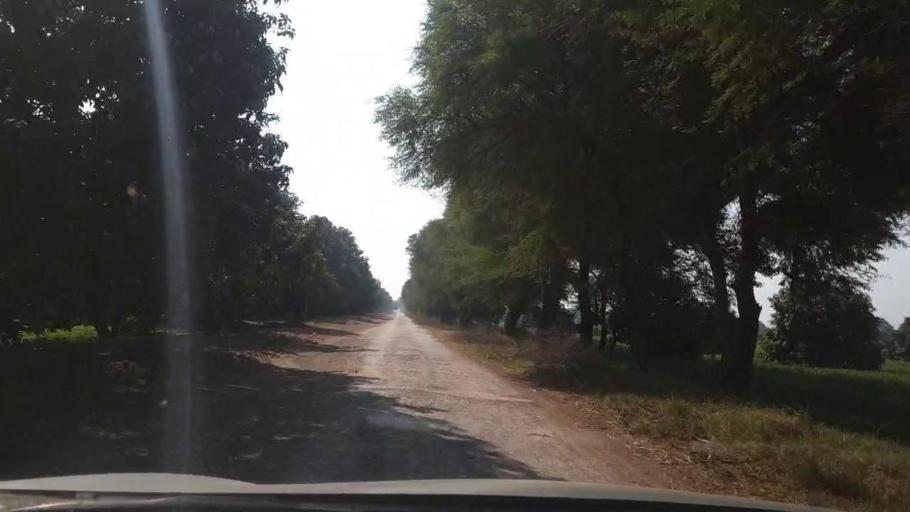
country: PK
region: Sindh
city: Tando Allahyar
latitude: 25.5141
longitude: 68.7861
